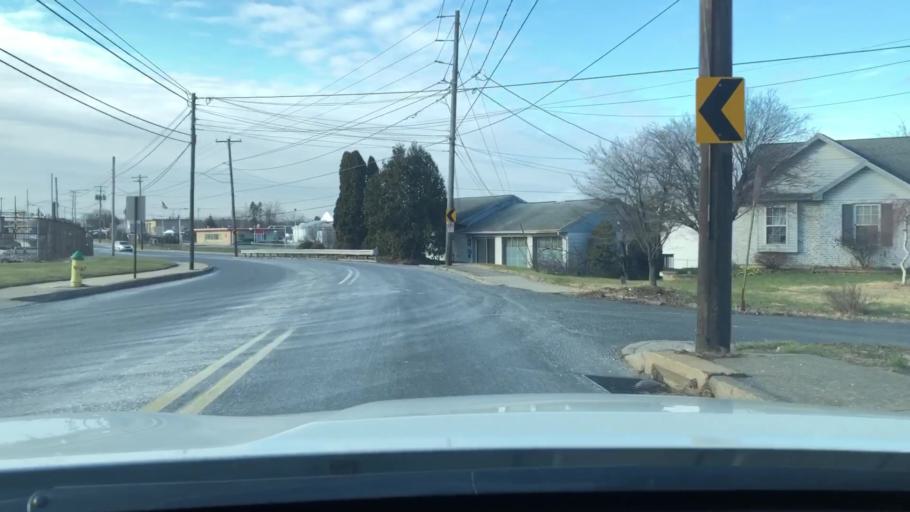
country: US
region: Pennsylvania
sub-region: Lehigh County
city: Catasauqua
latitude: 40.6453
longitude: -75.4811
